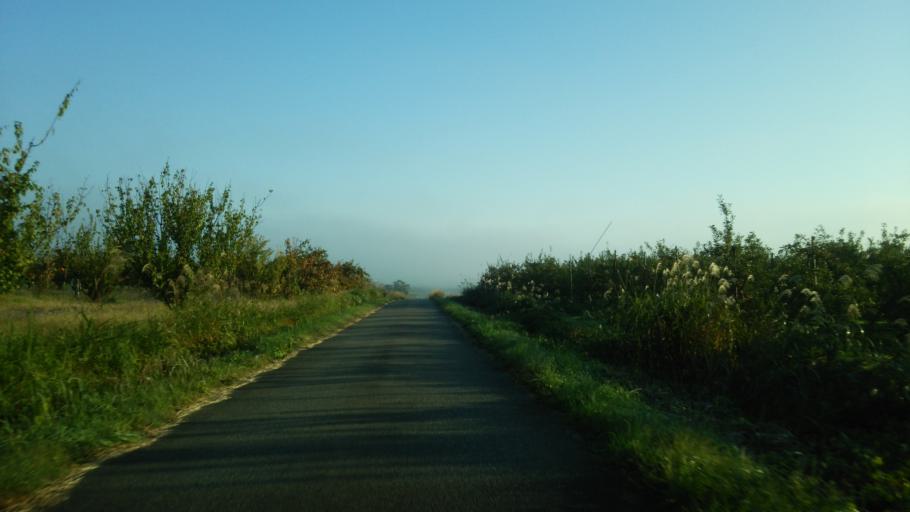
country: JP
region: Fukushima
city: Kitakata
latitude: 37.4395
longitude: 139.8038
